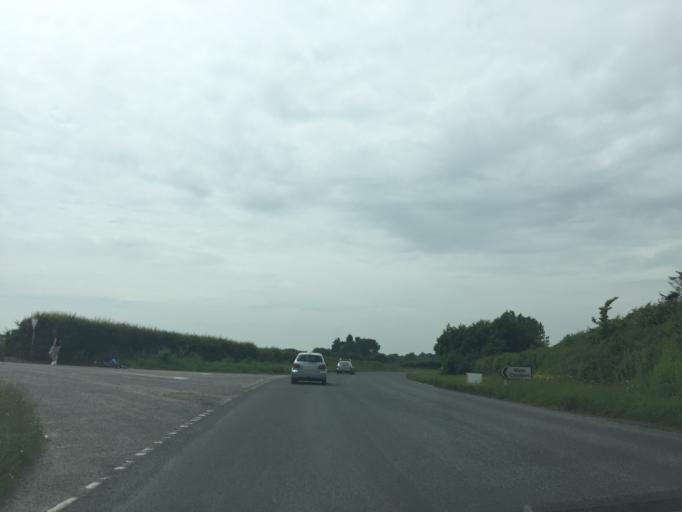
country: GB
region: England
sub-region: Dorset
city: Bovington Camp
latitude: 50.6633
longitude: -2.3156
